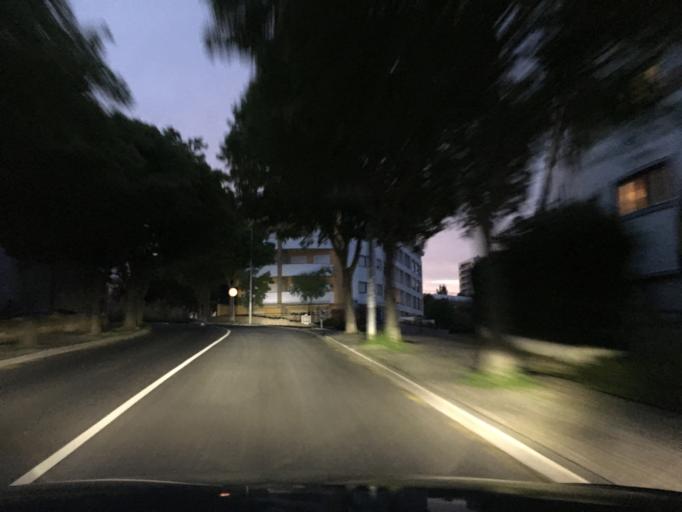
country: PT
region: Lisbon
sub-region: Oeiras
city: Paco de Arcos
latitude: 38.6990
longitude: -9.2951
